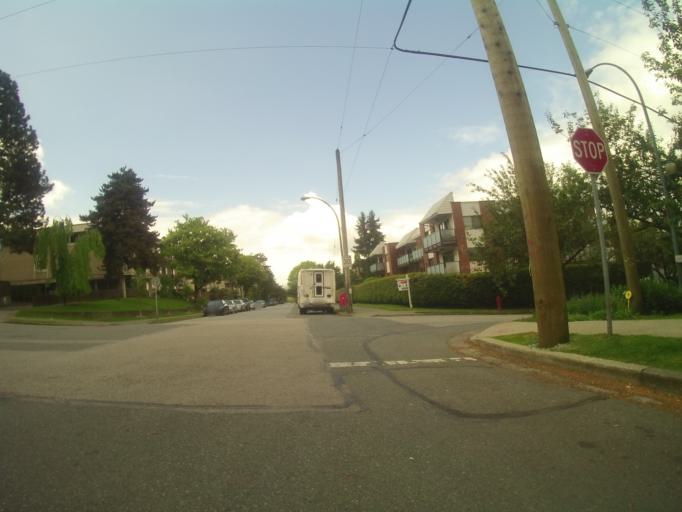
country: CA
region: British Columbia
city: Vancouver
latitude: 49.2652
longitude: -123.0887
